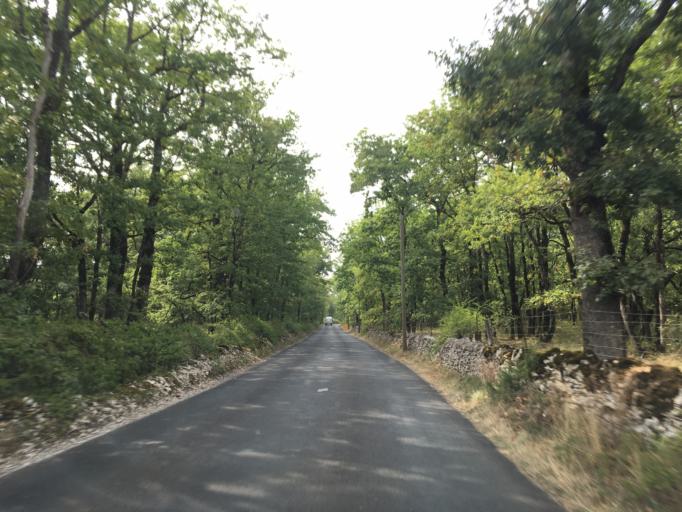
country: FR
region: Midi-Pyrenees
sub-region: Departement du Lot
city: Gramat
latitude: 44.8217
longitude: 1.6026
